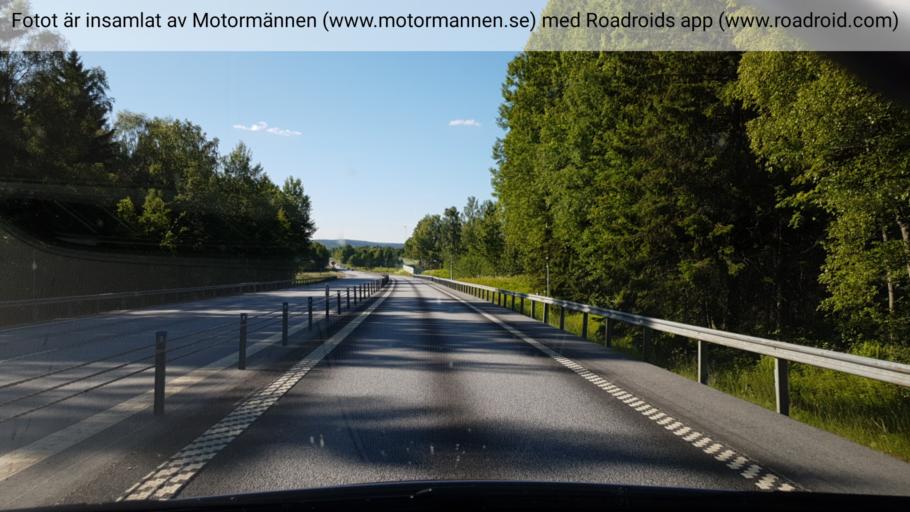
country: SE
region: Vaesterbotten
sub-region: Vannas Kommun
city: Vannasby
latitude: 63.9110
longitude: 19.8867
